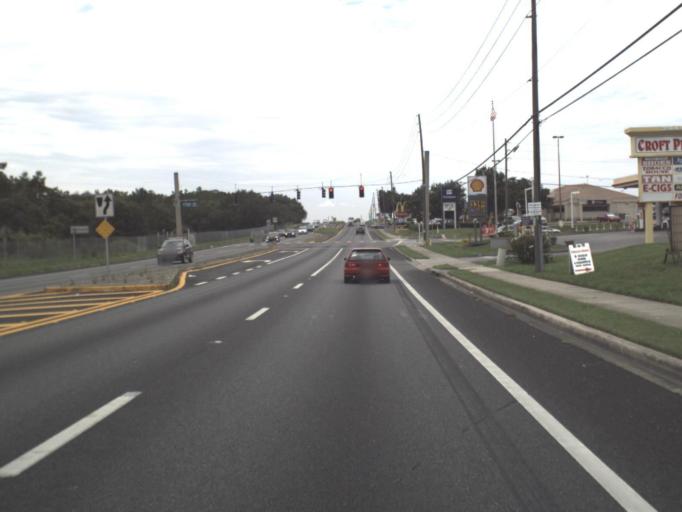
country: US
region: Florida
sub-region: Citrus County
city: Inverness Highlands North
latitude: 28.8529
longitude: -82.3850
